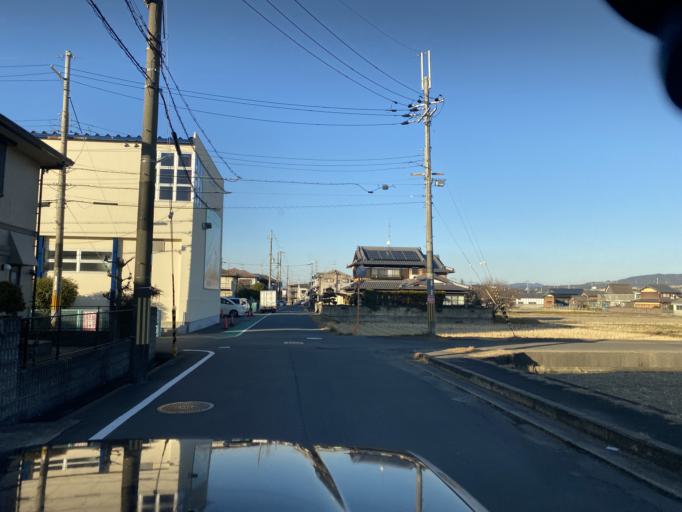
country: JP
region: Kyoto
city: Tanabe
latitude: 34.8156
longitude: 135.7808
